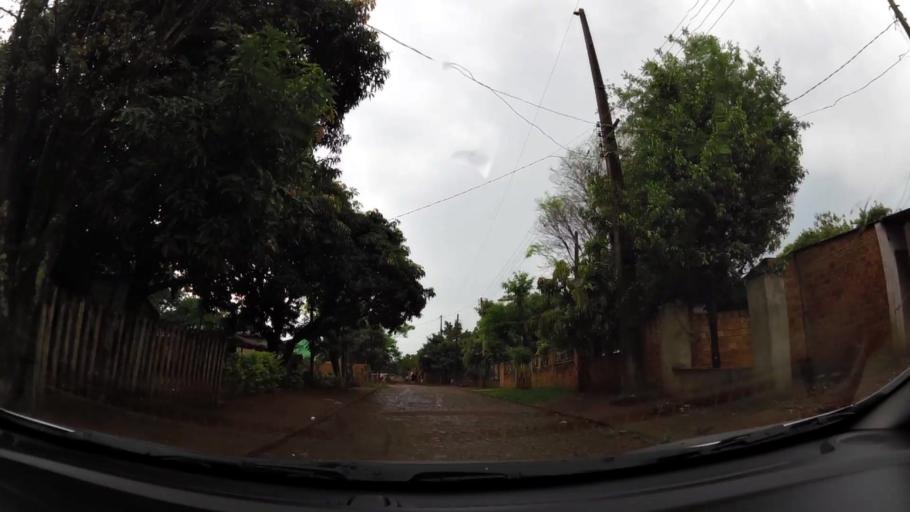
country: PY
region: Alto Parana
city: Presidente Franco
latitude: -25.5401
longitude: -54.6552
